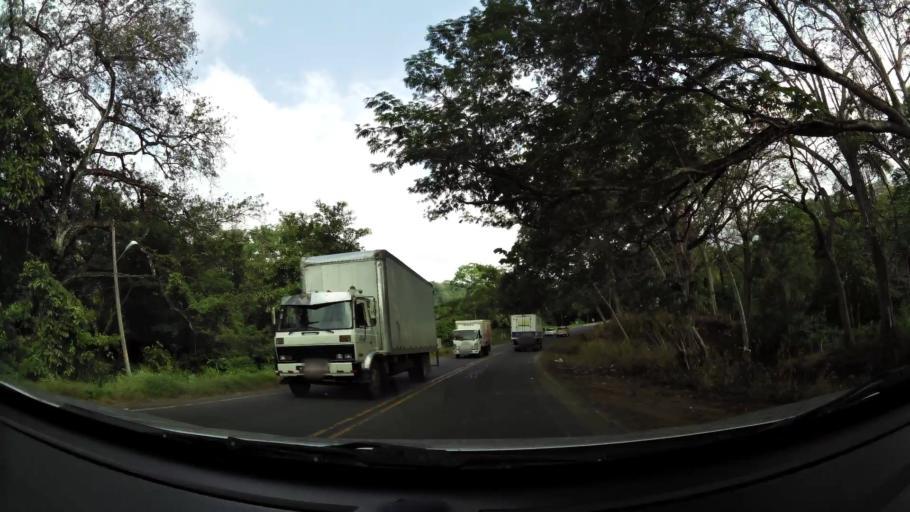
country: CR
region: Guanacaste
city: Juntas
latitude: 10.1850
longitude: -84.9414
